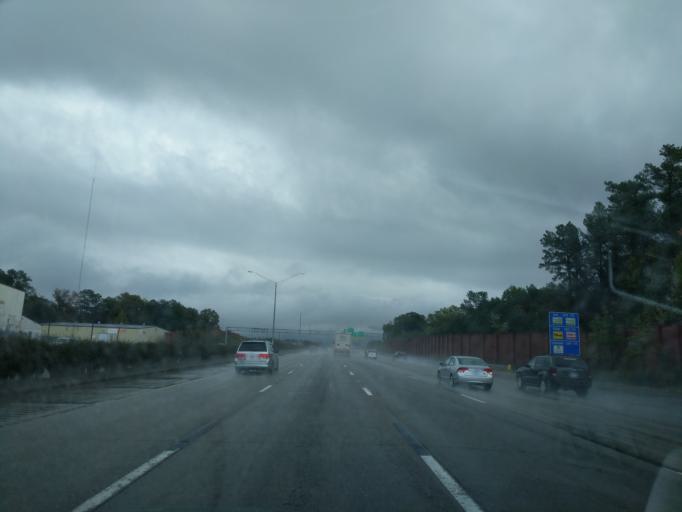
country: US
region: North Carolina
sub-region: Durham County
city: Durham
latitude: 36.0286
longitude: -78.9313
